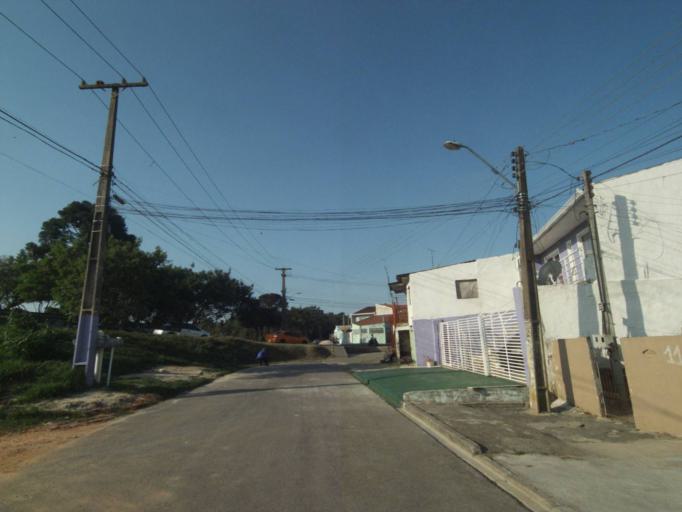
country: BR
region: Parana
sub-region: Curitiba
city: Curitiba
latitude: -25.4817
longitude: -49.3353
